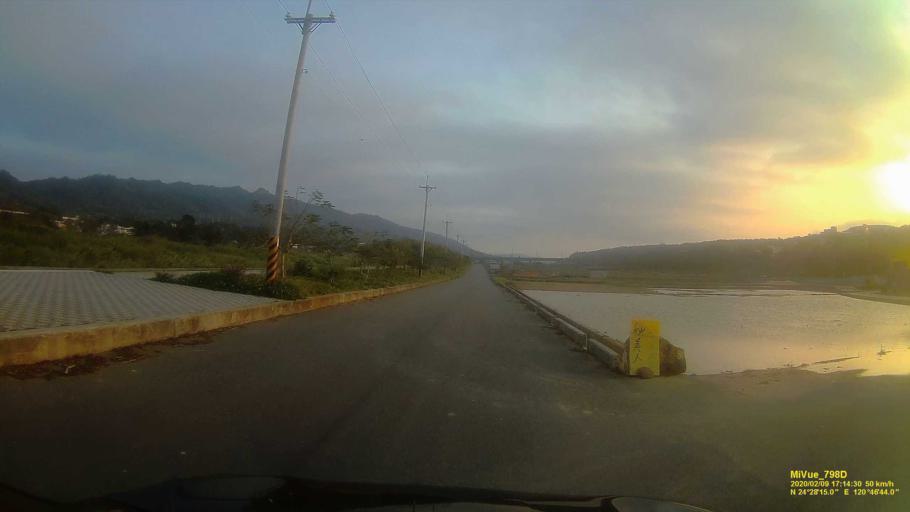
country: TW
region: Taiwan
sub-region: Miaoli
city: Miaoli
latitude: 24.4706
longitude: 120.7789
